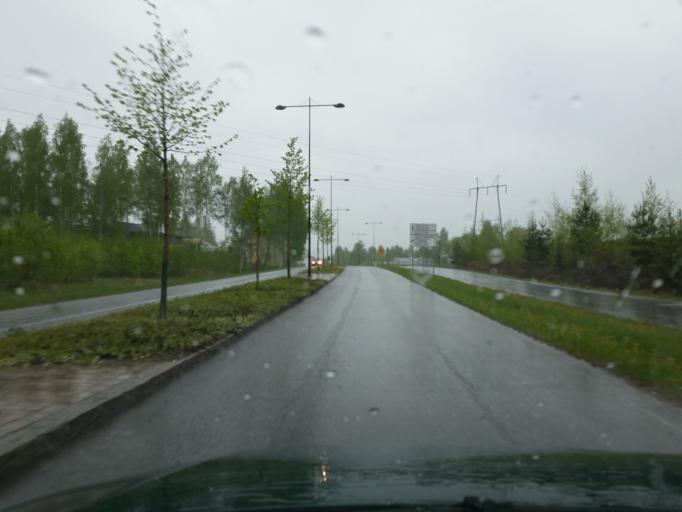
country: FI
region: Uusimaa
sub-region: Helsinki
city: Lohja
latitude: 60.2614
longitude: 24.0625
